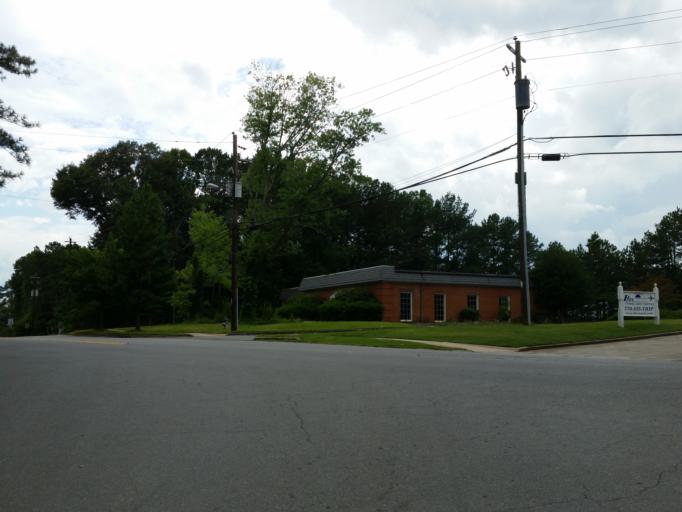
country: US
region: Georgia
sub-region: Cobb County
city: Kennesaw
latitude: 34.0224
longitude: -84.6174
